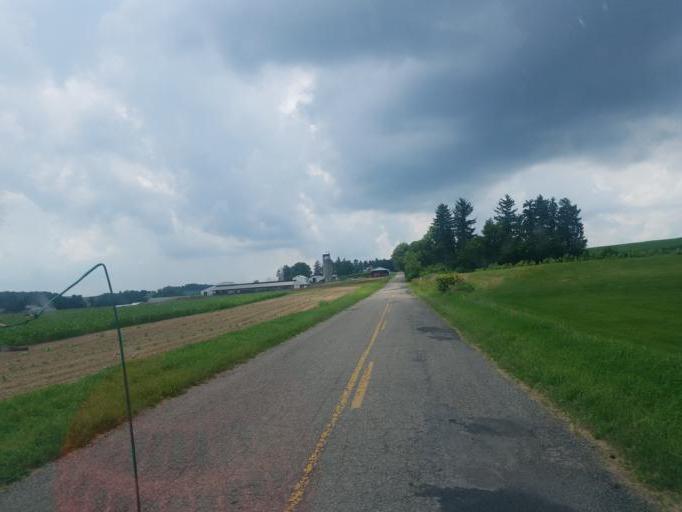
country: US
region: Ohio
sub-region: Columbiana County
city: Leetonia
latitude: 40.9237
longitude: -80.7390
